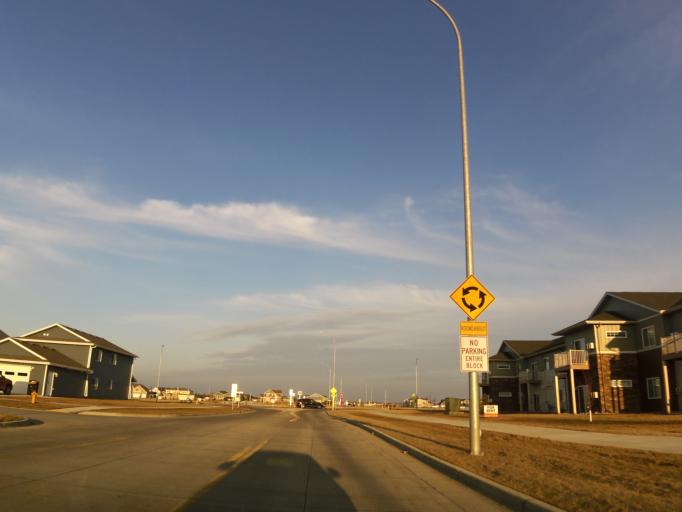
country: US
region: North Dakota
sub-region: Grand Forks County
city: Grand Forks
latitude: 47.8824
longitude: -97.0789
